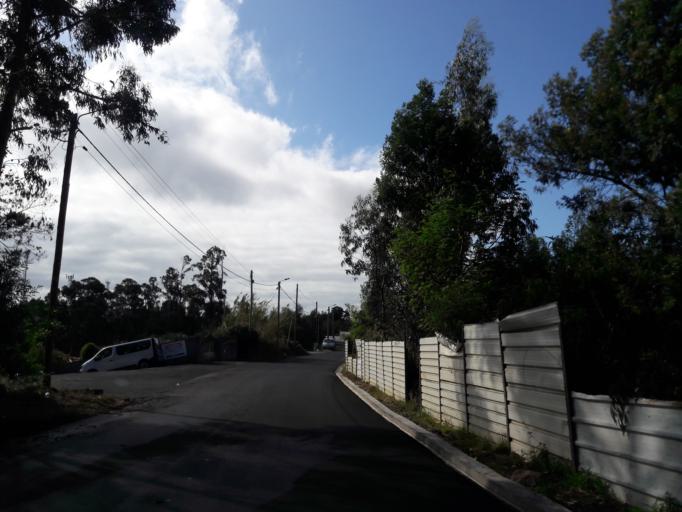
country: PT
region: Madeira
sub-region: Santa Cruz
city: Camacha
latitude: 32.6636
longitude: -16.8370
